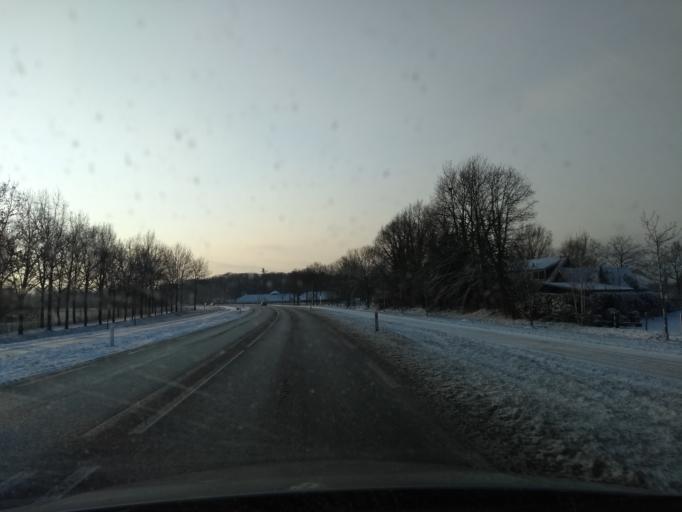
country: NL
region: Overijssel
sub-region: Gemeente Hof van Twente
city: Delden
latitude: 52.2933
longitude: 6.6618
